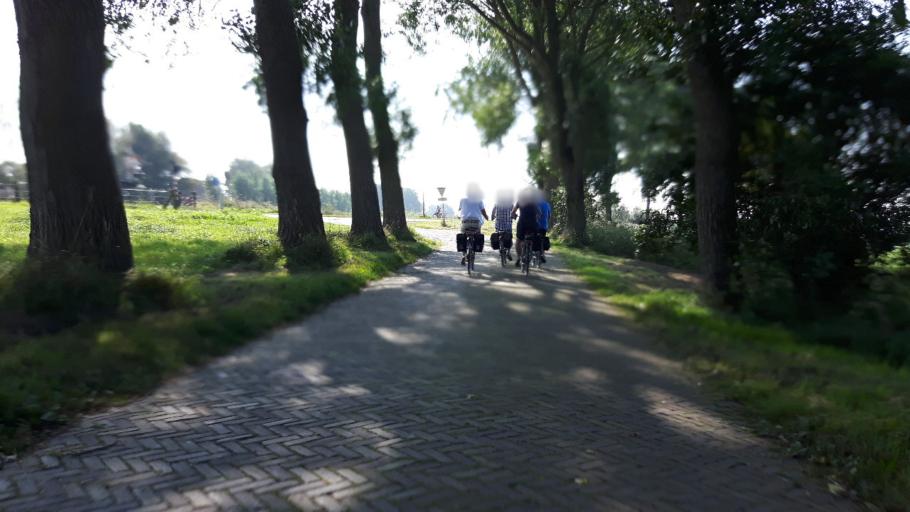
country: NL
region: Friesland
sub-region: Sudwest Fryslan
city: Koudum
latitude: 52.9450
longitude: 5.4210
